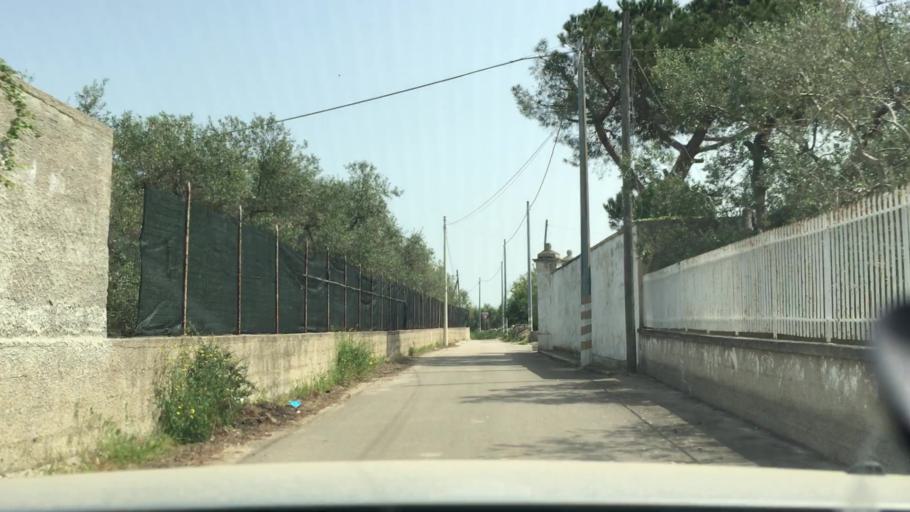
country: IT
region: Apulia
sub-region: Provincia di Barletta - Andria - Trani
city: Capirro
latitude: 41.2546
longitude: 16.4584
